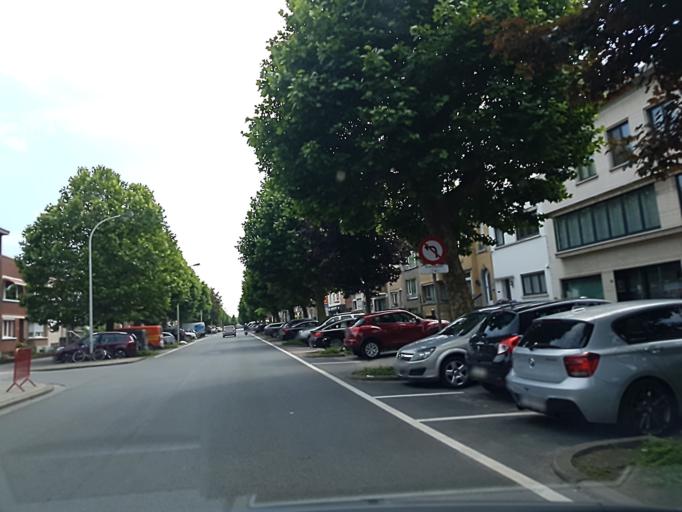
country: BE
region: Flanders
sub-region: Provincie Antwerpen
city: Borsbeek
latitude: 51.2279
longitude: 4.4707
